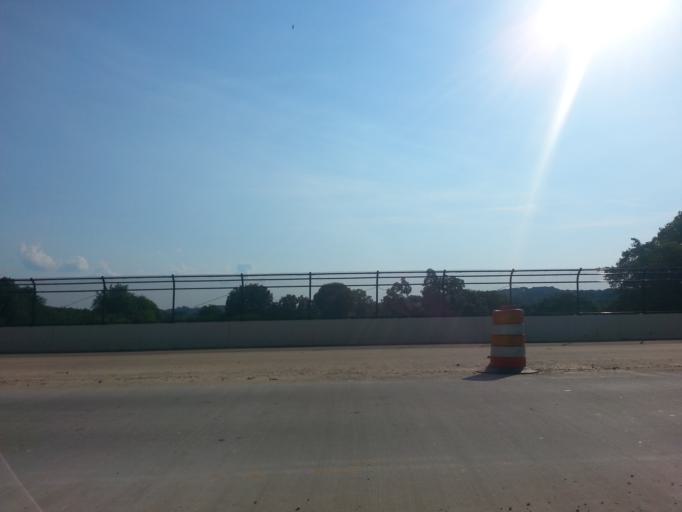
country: US
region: Tennessee
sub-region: Loudon County
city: Lenoir City
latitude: 35.7950
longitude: -84.2543
